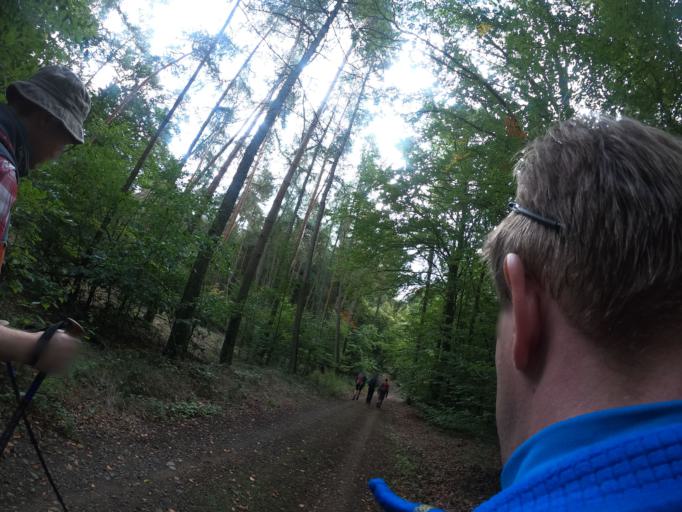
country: DE
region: Hesse
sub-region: Regierungsbezirk Darmstadt
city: Idstein
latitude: 50.2271
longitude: 8.2421
